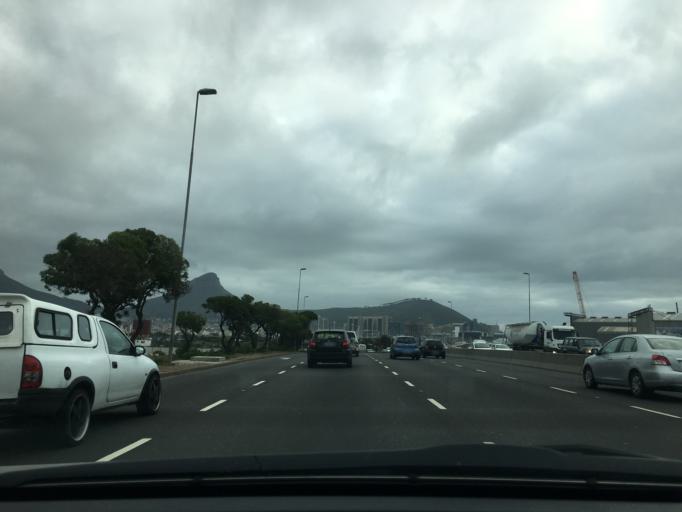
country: ZA
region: Western Cape
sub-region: City of Cape Town
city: Cape Town
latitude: -33.9215
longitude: 18.4526
